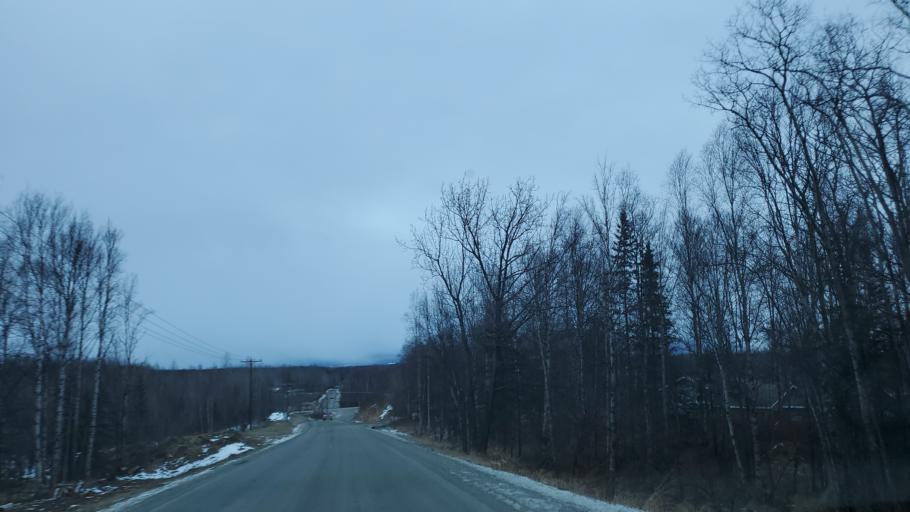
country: US
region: Alaska
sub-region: Matanuska-Susitna Borough
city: Farm Loop
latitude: 61.6572
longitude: -149.2254
